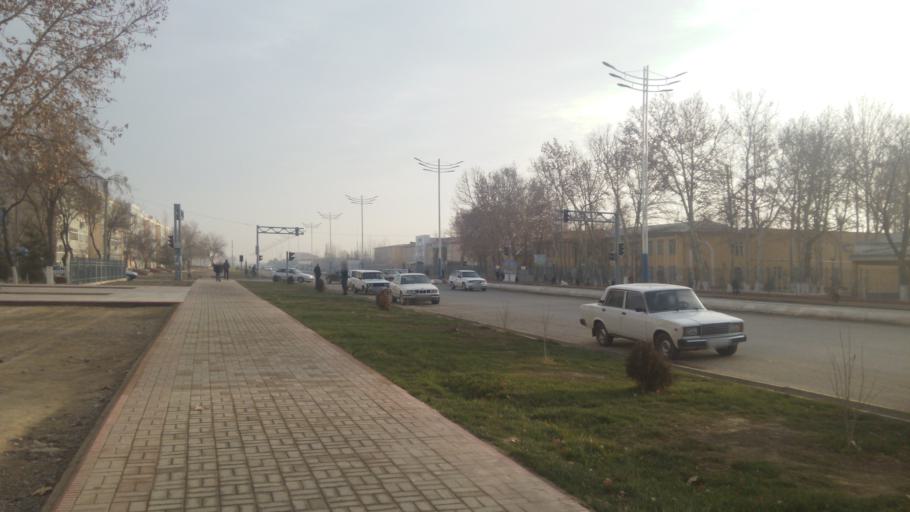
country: UZ
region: Sirdaryo
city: Guliston
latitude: 40.5127
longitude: 68.7805
